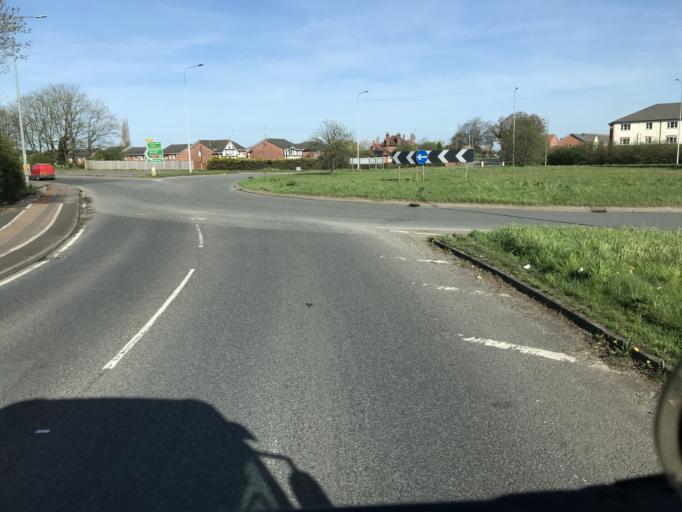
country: GB
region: England
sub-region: Cheshire West and Chester
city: Marston
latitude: 53.2499
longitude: -2.4730
